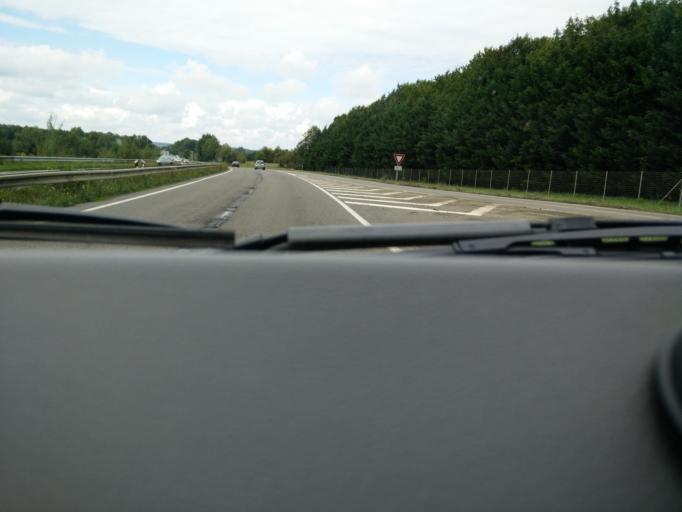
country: FR
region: Champagne-Ardenne
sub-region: Departement des Ardennes
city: Tournes
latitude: 49.7982
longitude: 4.6306
